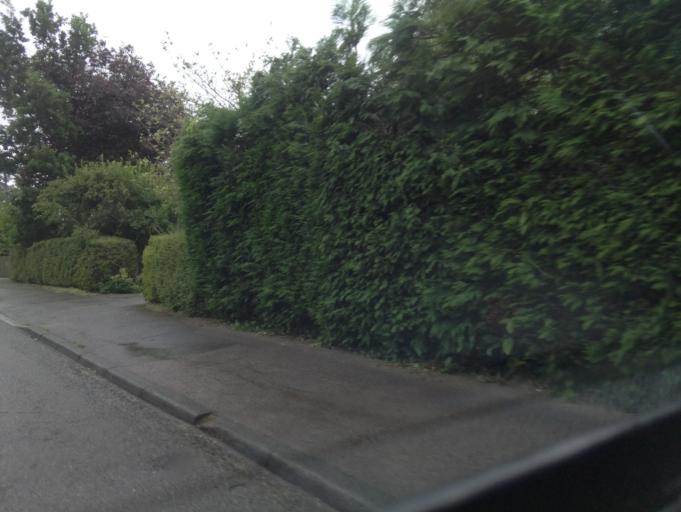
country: GB
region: England
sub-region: Surrey
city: Reigate
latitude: 51.2457
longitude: -0.1916
